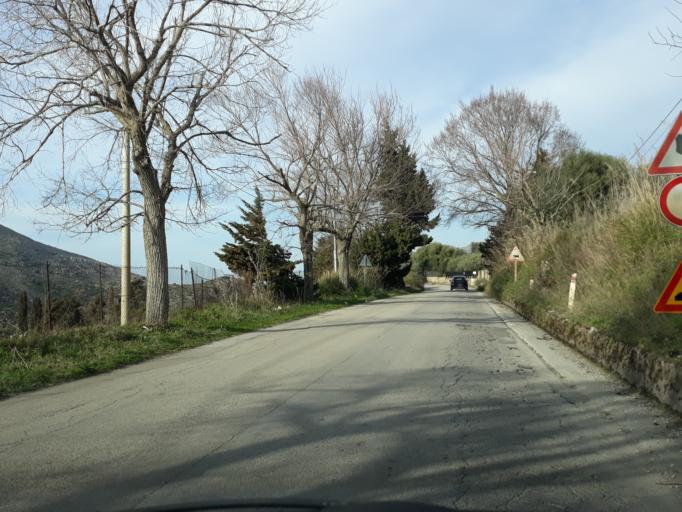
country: IT
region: Sicily
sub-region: Palermo
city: Torretta
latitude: 38.1044
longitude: 13.2334
